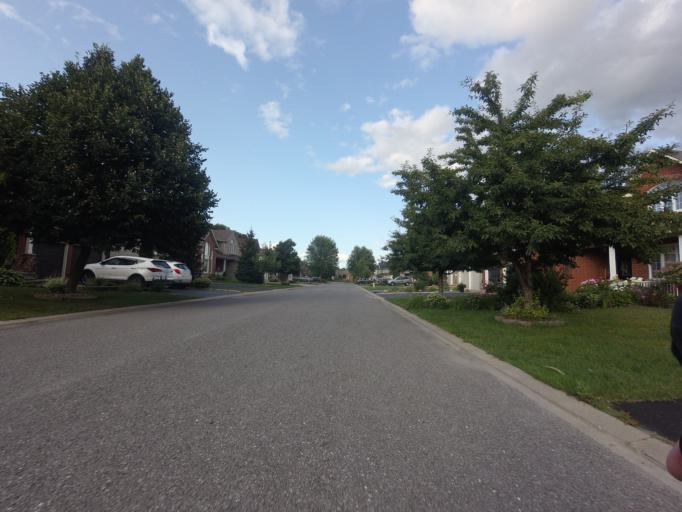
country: CA
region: Ontario
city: Bells Corners
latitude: 45.2896
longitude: -75.7183
